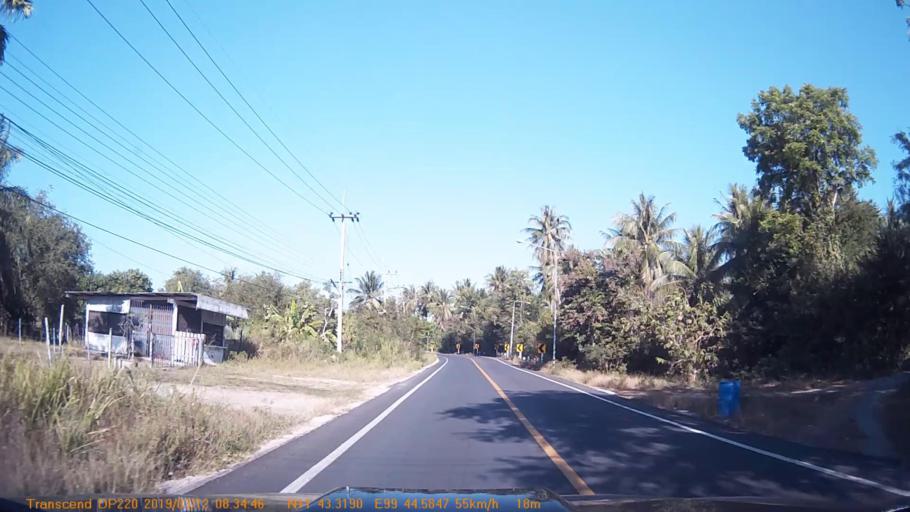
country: TH
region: Prachuap Khiri Khan
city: Prachuap Khiri Khan
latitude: 11.7222
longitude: 99.7427
